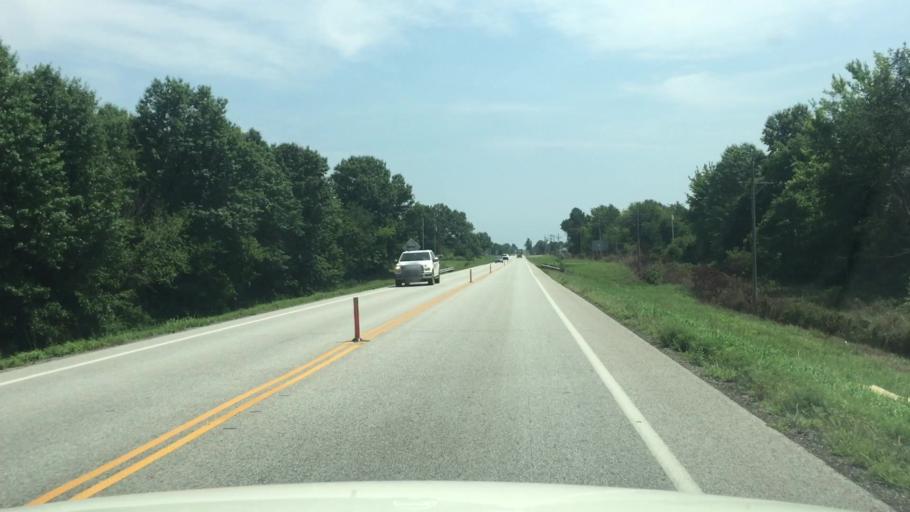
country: US
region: Kansas
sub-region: Cherokee County
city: Columbus
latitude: 37.1781
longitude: -94.8202
